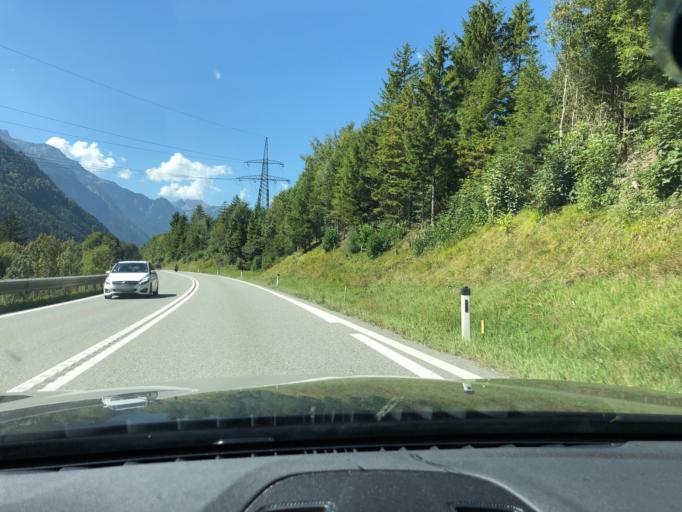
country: AT
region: Vorarlberg
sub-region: Politischer Bezirk Bludenz
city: Innerbraz
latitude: 47.1461
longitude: 9.8971
